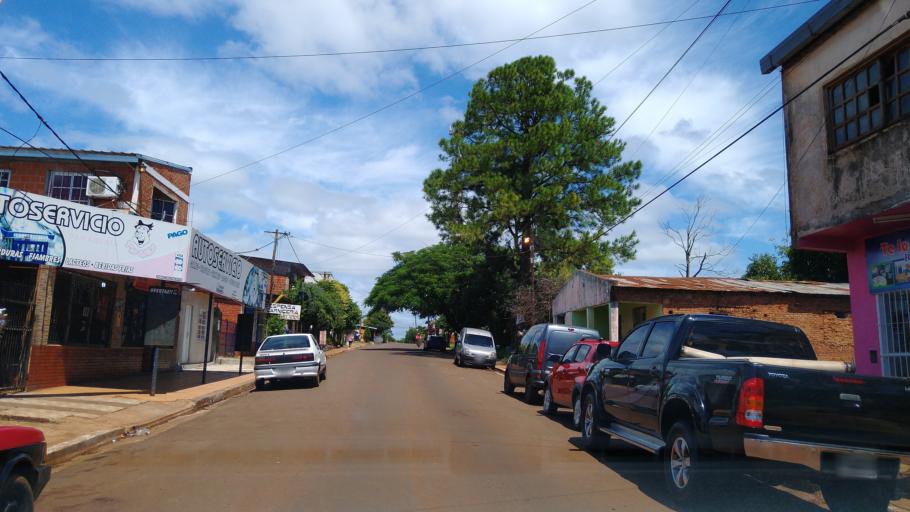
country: AR
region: Misiones
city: Garupa
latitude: -27.4563
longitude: -55.8587
